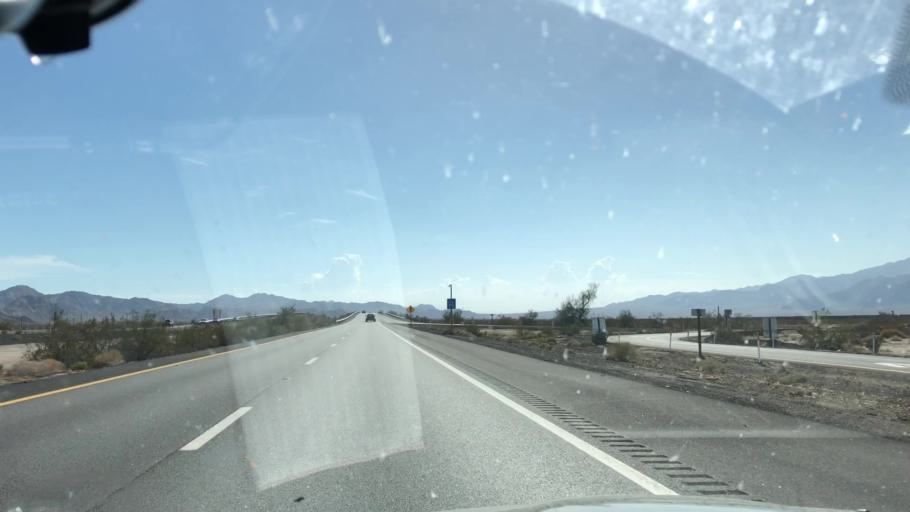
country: US
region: California
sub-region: Imperial County
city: Niland
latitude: 33.6781
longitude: -115.5624
